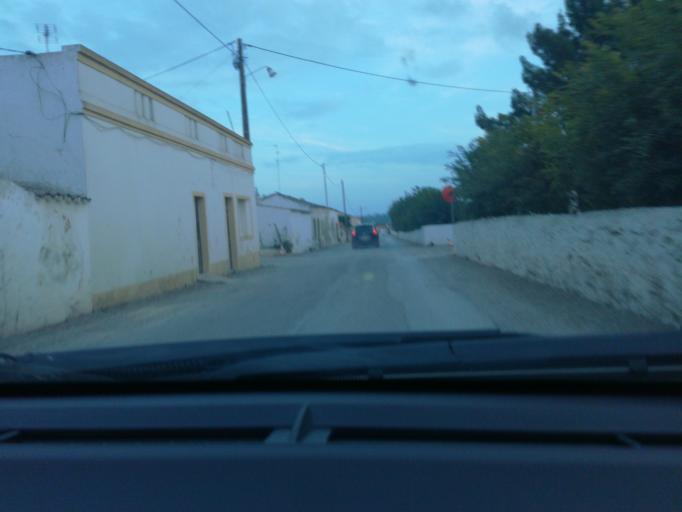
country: PT
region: Faro
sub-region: Olhao
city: Moncarapacho
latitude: 37.0813
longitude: -7.7818
